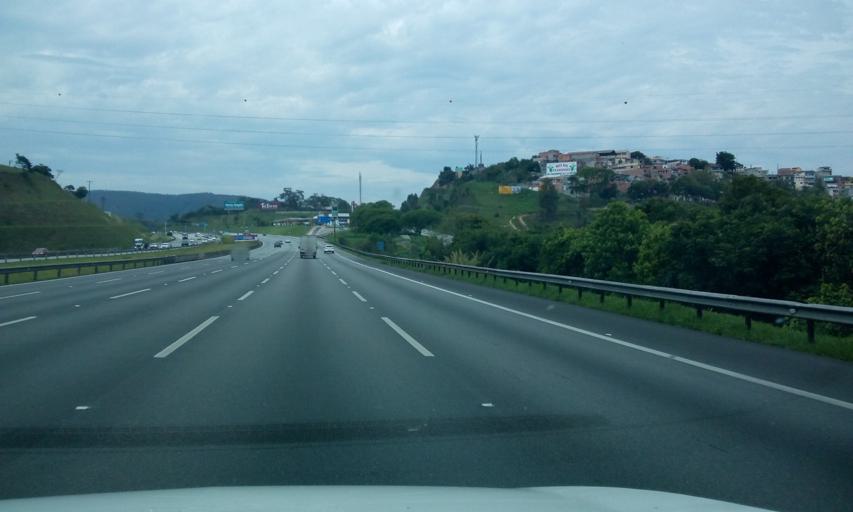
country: BR
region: Sao Paulo
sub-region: Cajamar
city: Cajamar
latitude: -23.3305
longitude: -46.8237
